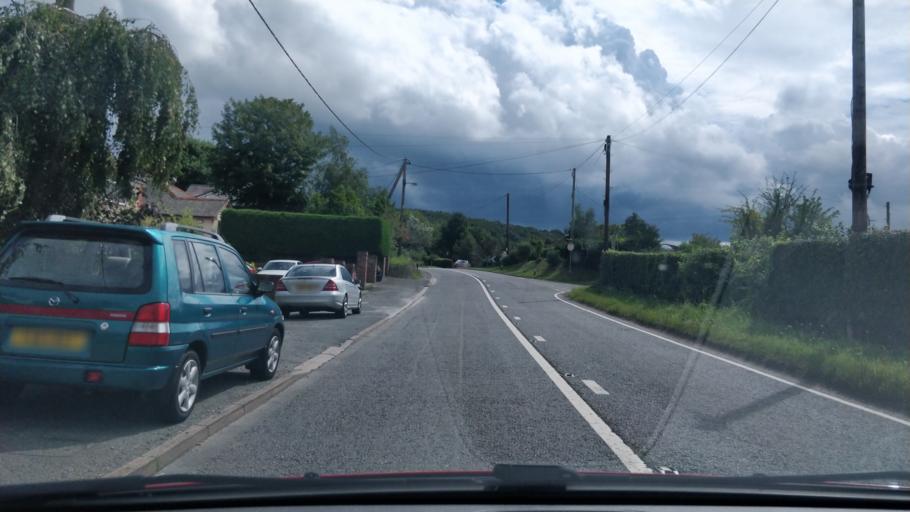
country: GB
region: Wales
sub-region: County of Flintshire
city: Hope
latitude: 53.1161
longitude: -3.0302
